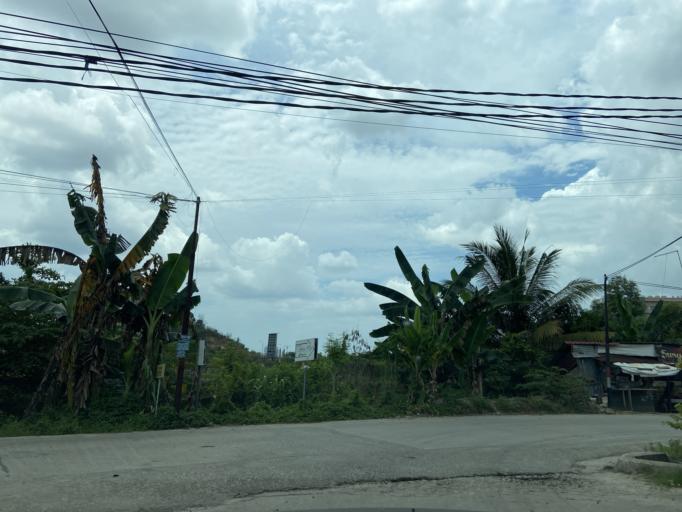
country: SG
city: Singapore
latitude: 1.1256
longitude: 104.0154
